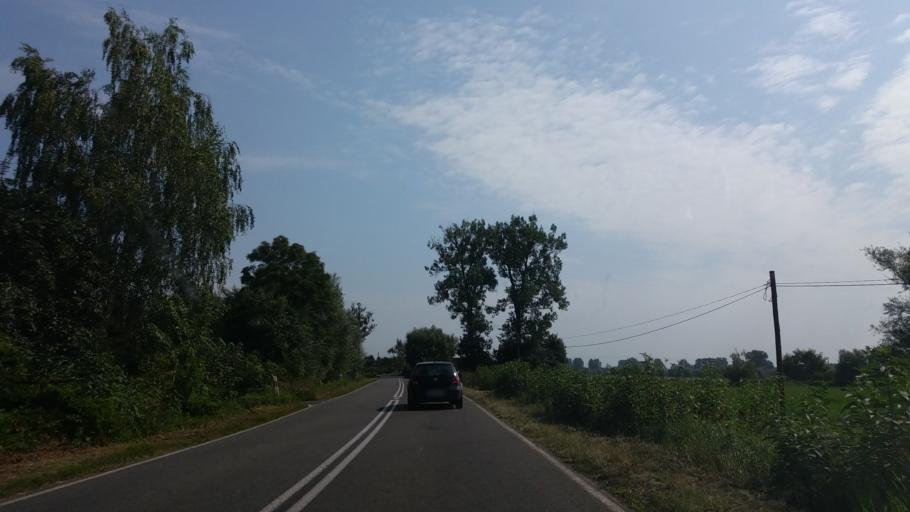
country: PL
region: Lubusz
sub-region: Powiat strzelecko-drezdenecki
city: Zwierzyn
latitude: 52.8228
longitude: 15.6146
